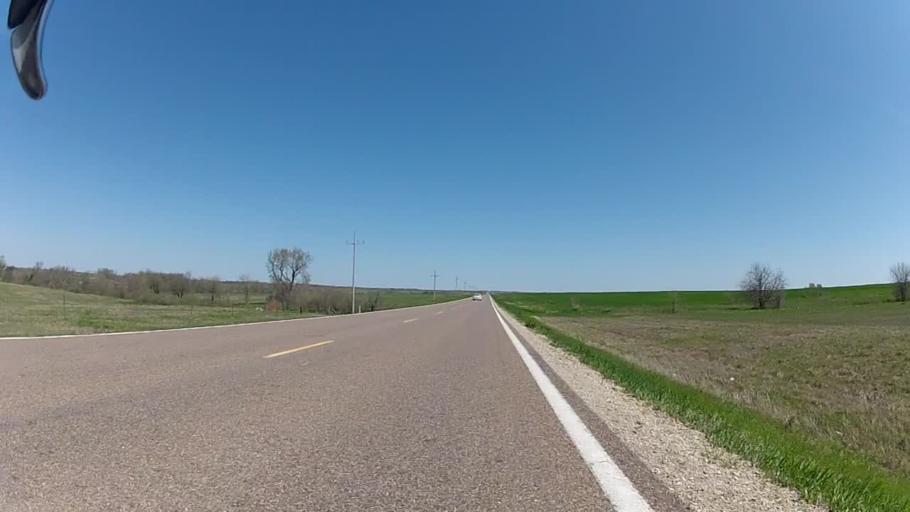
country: US
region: Kansas
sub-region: Morris County
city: Council Grove
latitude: 38.8944
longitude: -96.5202
